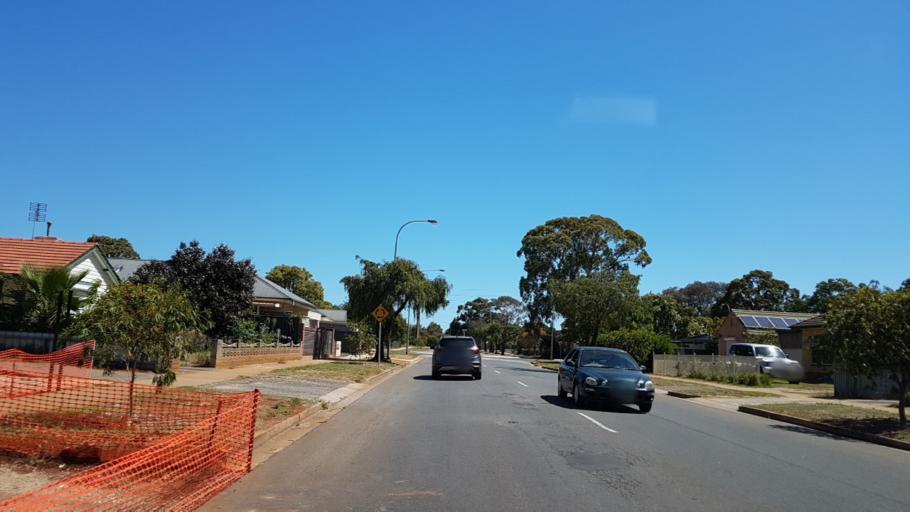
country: AU
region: South Australia
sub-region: Salisbury
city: Elizabeth
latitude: -34.7315
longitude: 138.6597
